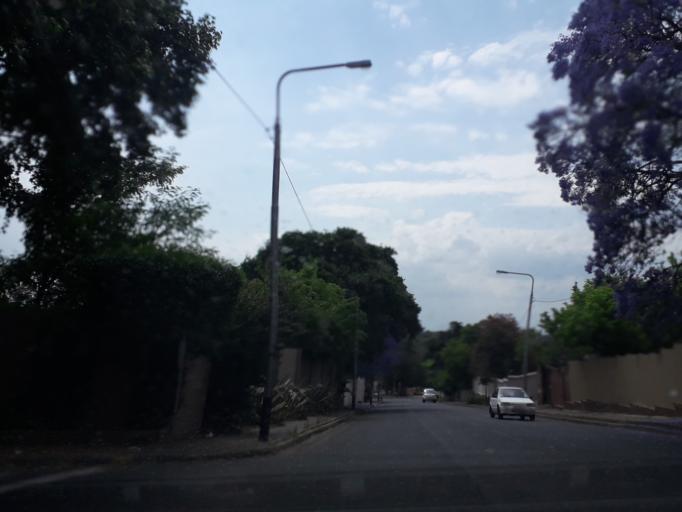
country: ZA
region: Gauteng
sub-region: City of Johannesburg Metropolitan Municipality
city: Johannesburg
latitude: -26.1636
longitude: 28.0206
